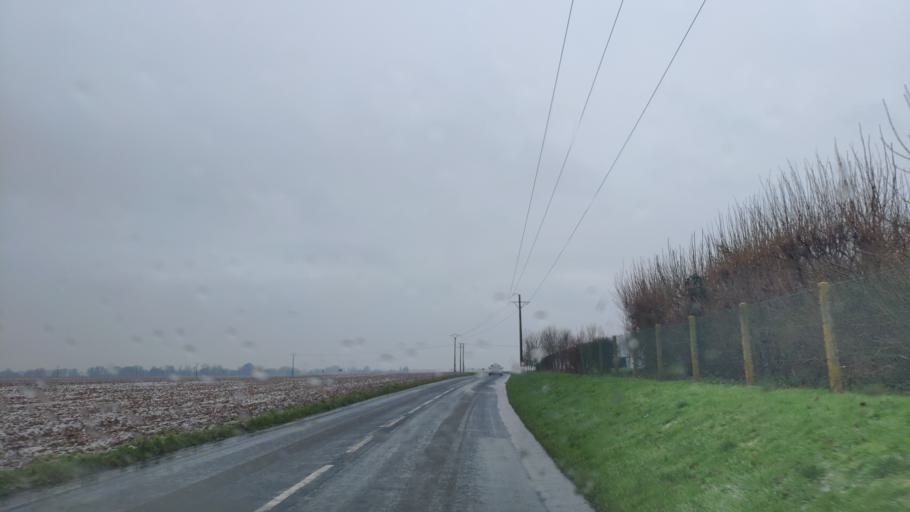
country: FR
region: Haute-Normandie
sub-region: Departement de la Seine-Maritime
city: Cany-Barville
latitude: 49.7902
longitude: 0.6539
